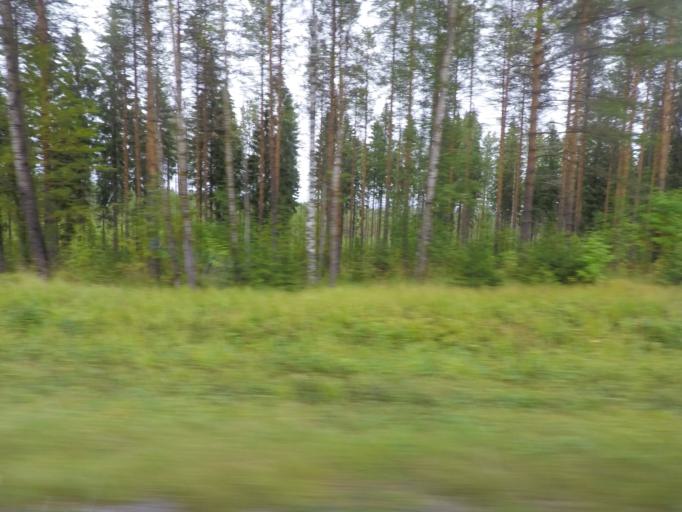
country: FI
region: Southern Savonia
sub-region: Pieksaemaeki
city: Juva
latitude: 62.0099
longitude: 27.8008
